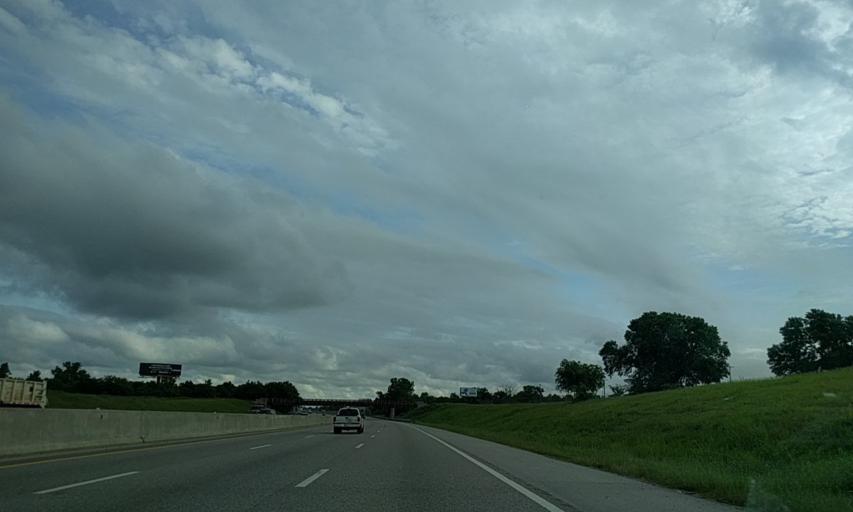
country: US
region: Oklahoma
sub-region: Tulsa County
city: Owasso
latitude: 36.1831
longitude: -95.8528
